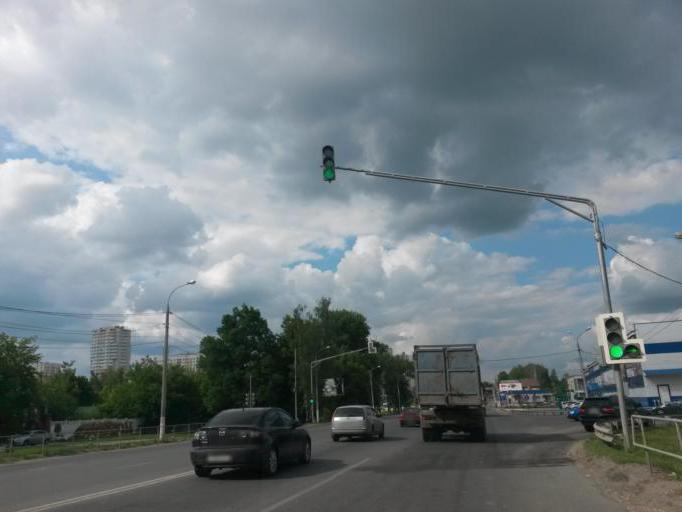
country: RU
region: Moskovskaya
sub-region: Chekhovskiy Rayon
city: Chekhov
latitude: 55.1627
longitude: 37.4665
